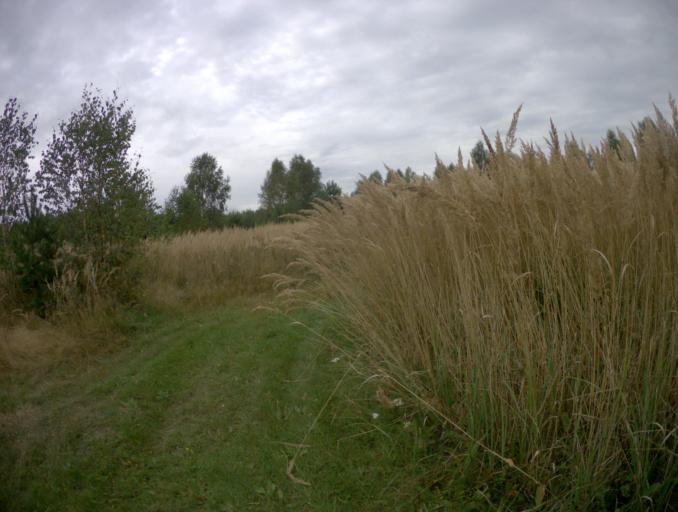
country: RU
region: Vladimir
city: Urshel'skiy
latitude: 55.8531
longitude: 40.2089
